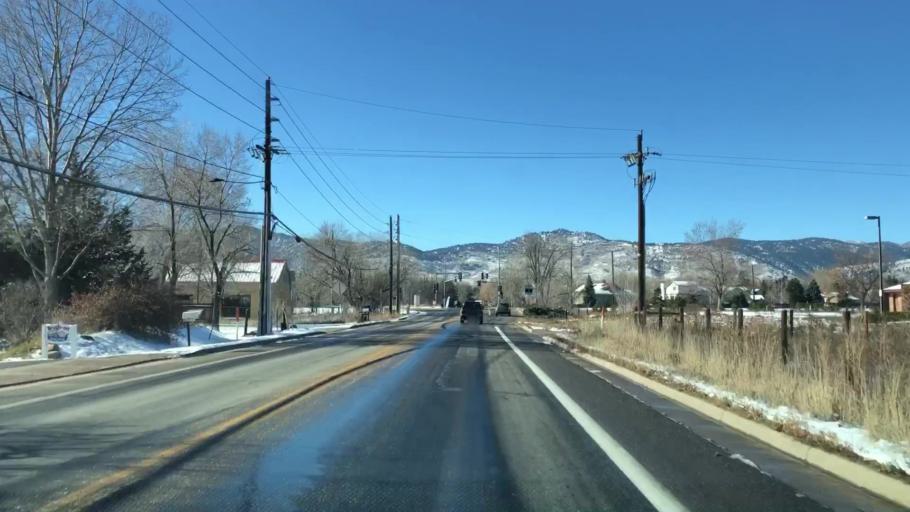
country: US
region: Colorado
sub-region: Boulder County
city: Boulder
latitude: 40.0510
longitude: -105.2580
